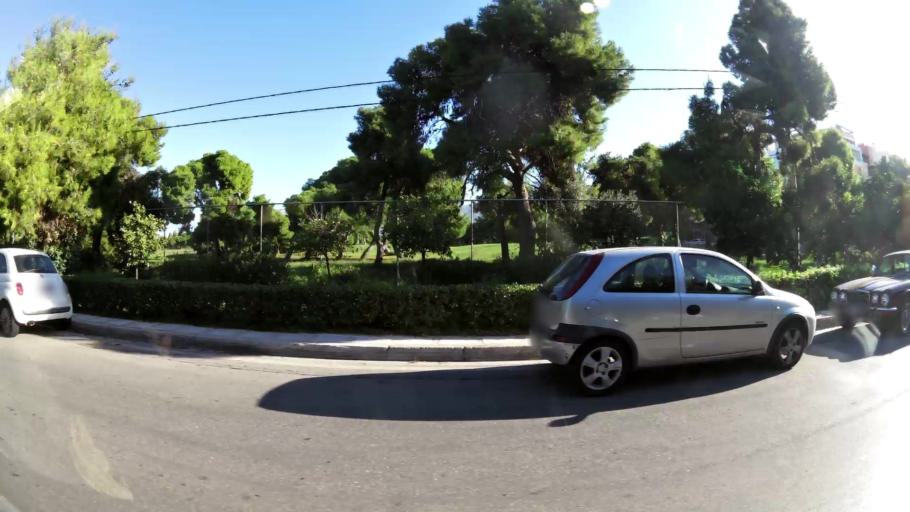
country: GR
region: Attica
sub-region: Nomarchia Athinas
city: Glyfada
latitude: 37.8676
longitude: 23.7444
